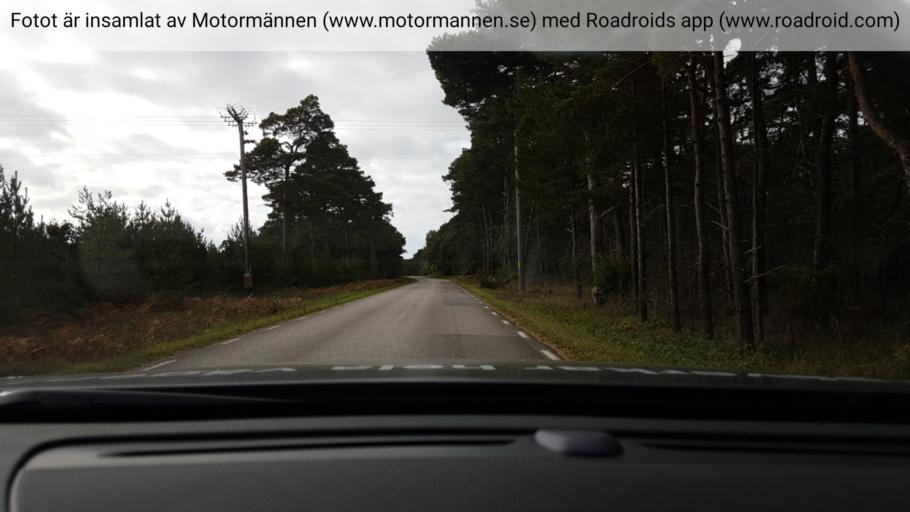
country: SE
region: Gotland
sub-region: Gotland
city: Hemse
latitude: 56.9565
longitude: 18.2153
